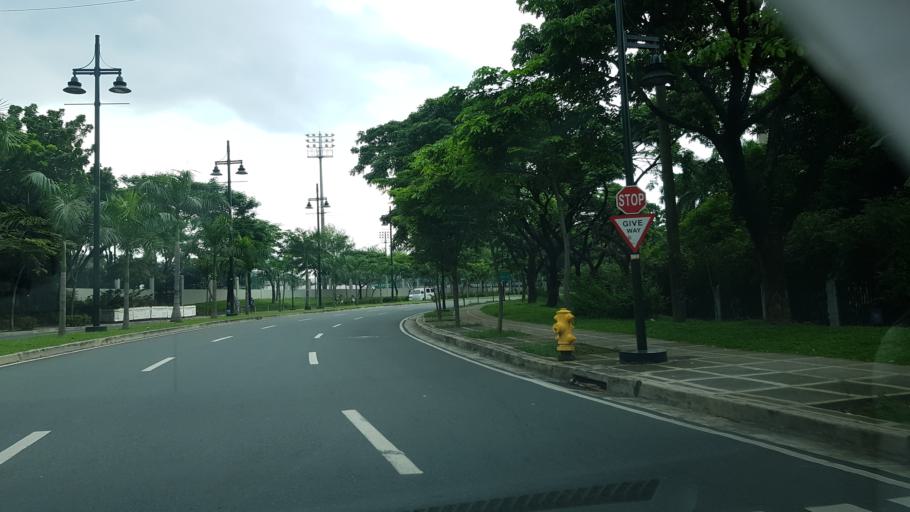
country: PH
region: Calabarzon
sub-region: Province of Rizal
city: Pateros
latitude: 14.5575
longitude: 121.0589
